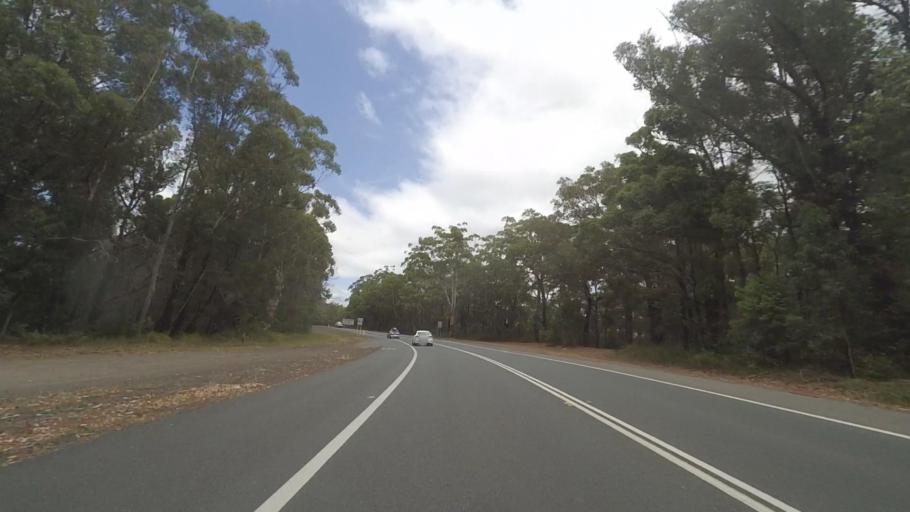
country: AU
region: New South Wales
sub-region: Shoalhaven Shire
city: Milton
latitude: -35.1457
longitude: 150.4613
